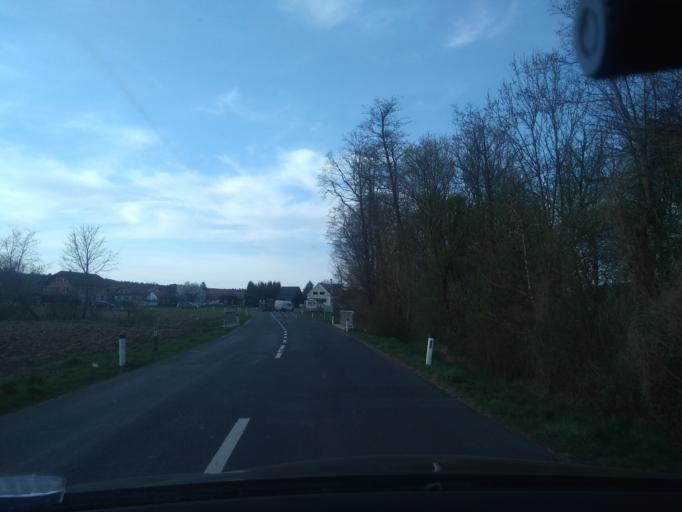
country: AT
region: Styria
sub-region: Politischer Bezirk Suedoststeiermark
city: Sankt Peter am Ottersbach
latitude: 46.7741
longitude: 15.7686
